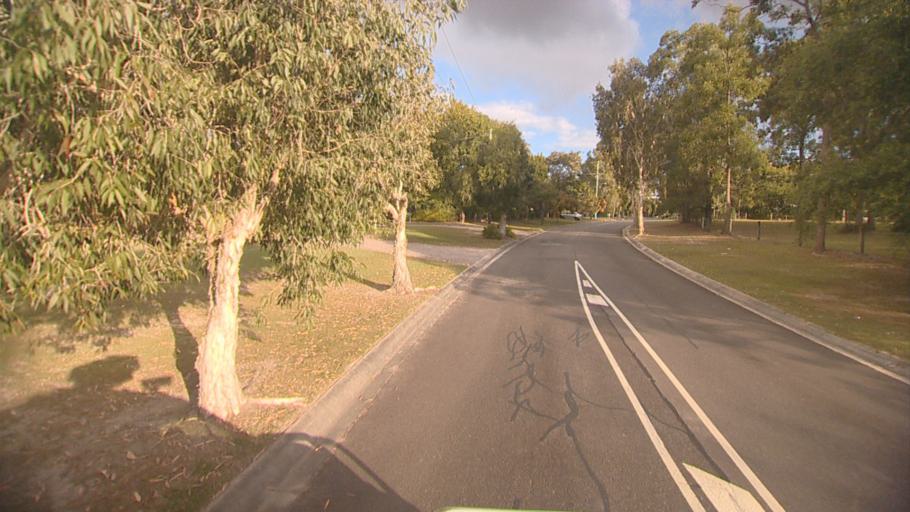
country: AU
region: Queensland
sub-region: Logan
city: Park Ridge South
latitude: -27.7039
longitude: 153.0207
